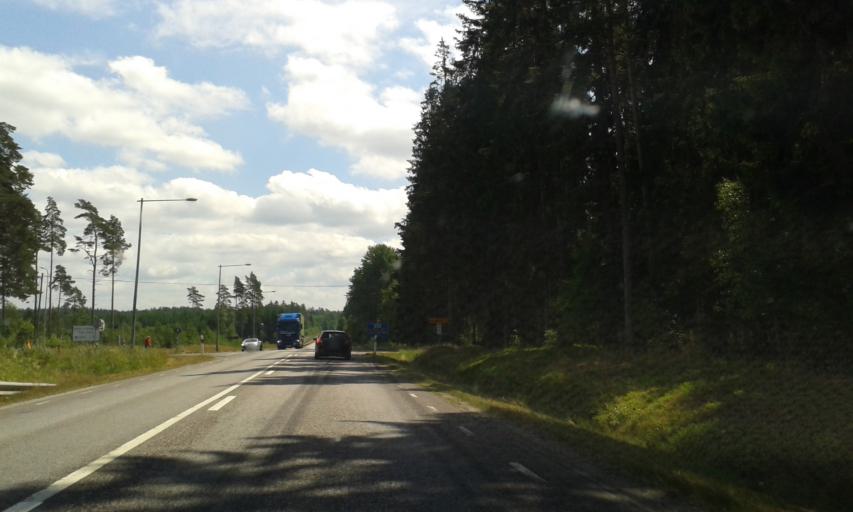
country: SE
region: Joenkoeping
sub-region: Varnamo Kommun
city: Rydaholm
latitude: 56.9746
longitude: 14.3151
